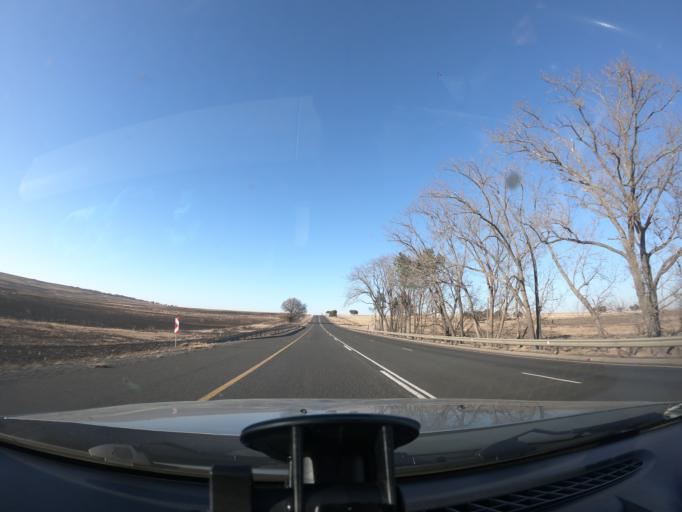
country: ZA
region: Mpumalanga
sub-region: Gert Sibande District Municipality
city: Ermelo
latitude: -26.4497
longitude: 29.9494
